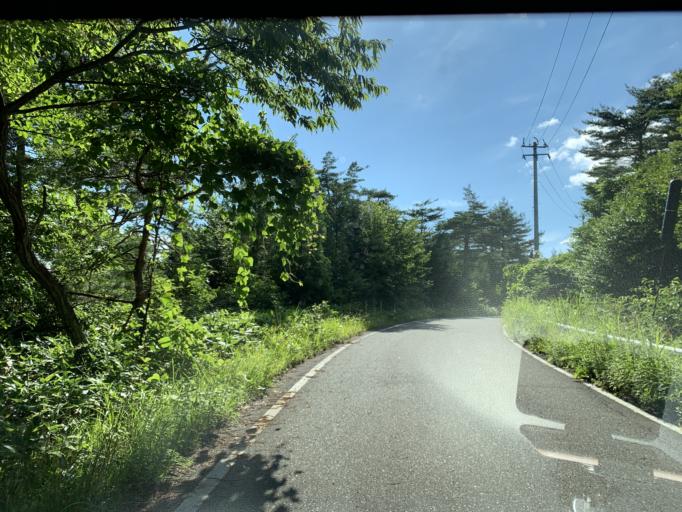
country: JP
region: Iwate
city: Ichinoseki
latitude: 38.8931
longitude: 140.8977
